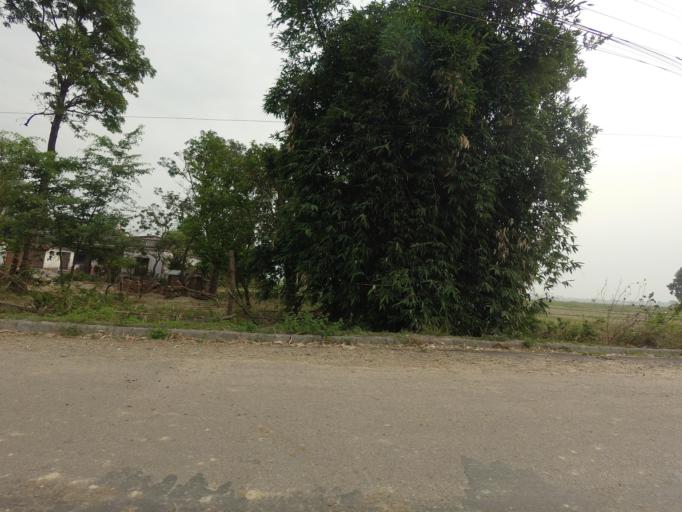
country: NP
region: Western Region
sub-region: Lumbini Zone
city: Bhairahawa
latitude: 27.4895
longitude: 83.4313
